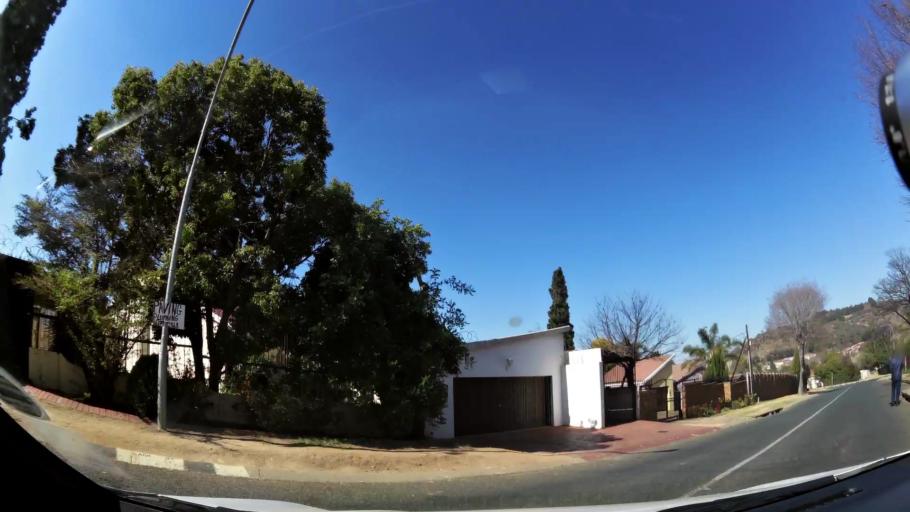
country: ZA
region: Gauteng
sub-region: City of Johannesburg Metropolitan Municipality
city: Johannesburg
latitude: -26.2737
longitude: 27.9871
